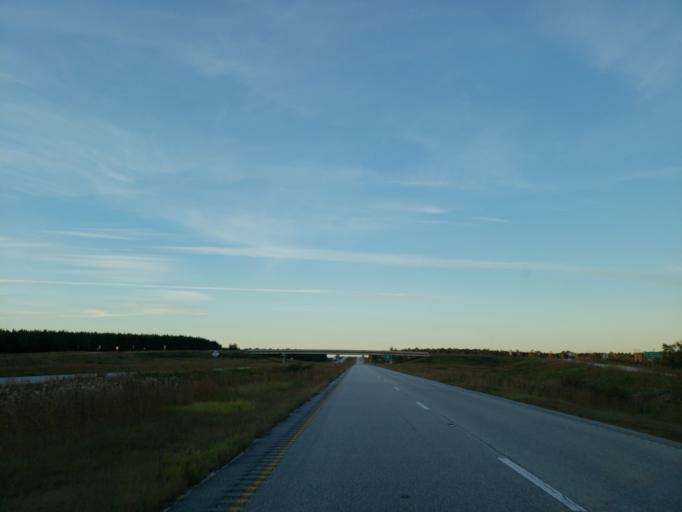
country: US
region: Mississippi
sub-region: Wayne County
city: Belmont
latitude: 31.4334
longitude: -88.4656
